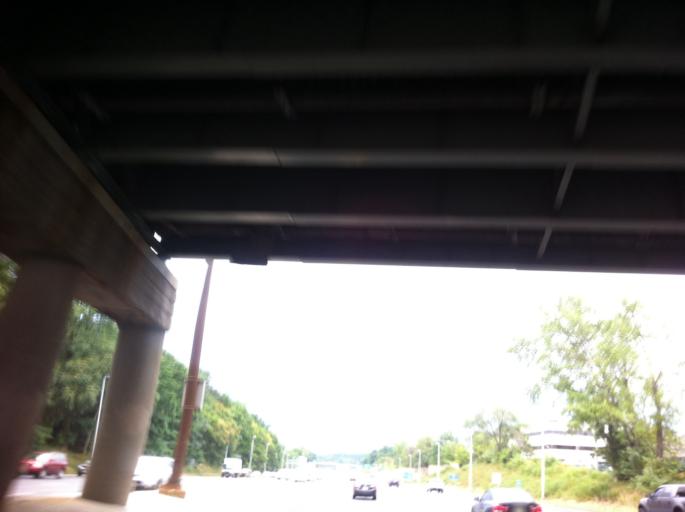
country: US
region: New Jersey
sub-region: Morris County
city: Parsippany
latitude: 40.8606
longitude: -74.3919
